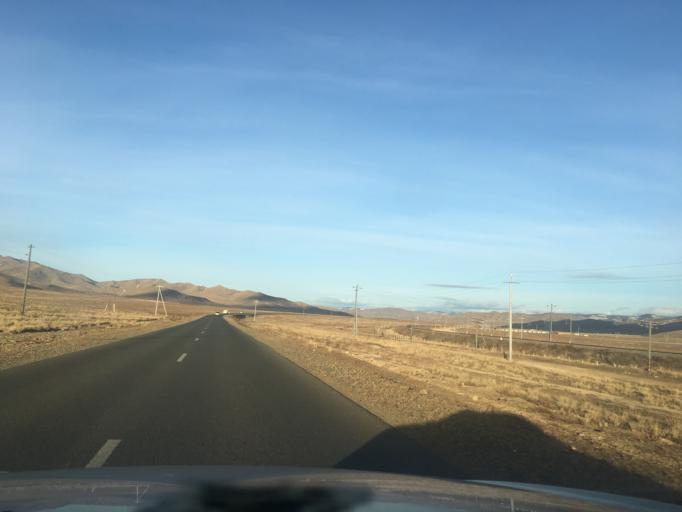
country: MN
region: Central Aimak
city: Ihsueuej
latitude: 48.0792
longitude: 106.5835
